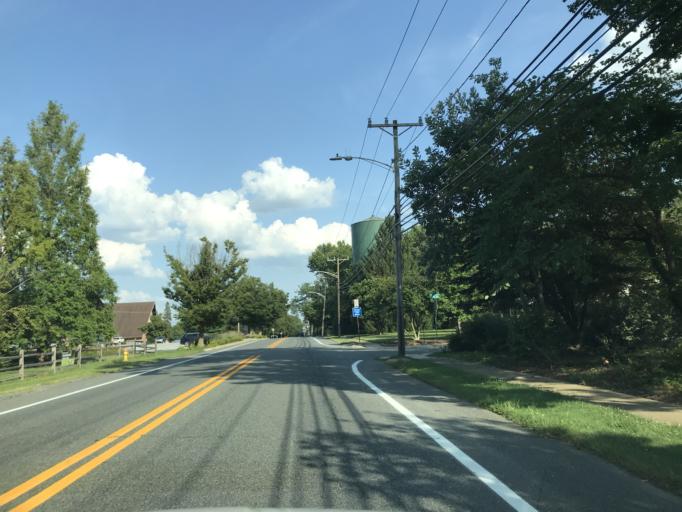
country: US
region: Delaware
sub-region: New Castle County
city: Newark
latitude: 39.6867
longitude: -75.7661
